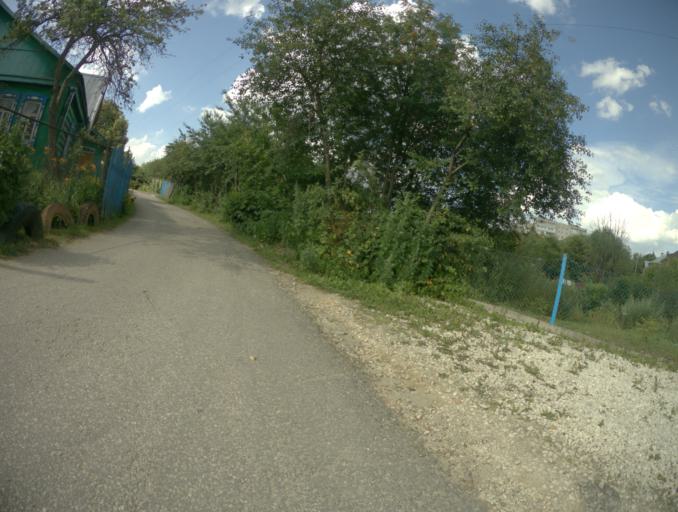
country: RU
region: Vladimir
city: Vladimir
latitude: 56.1154
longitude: 40.3711
